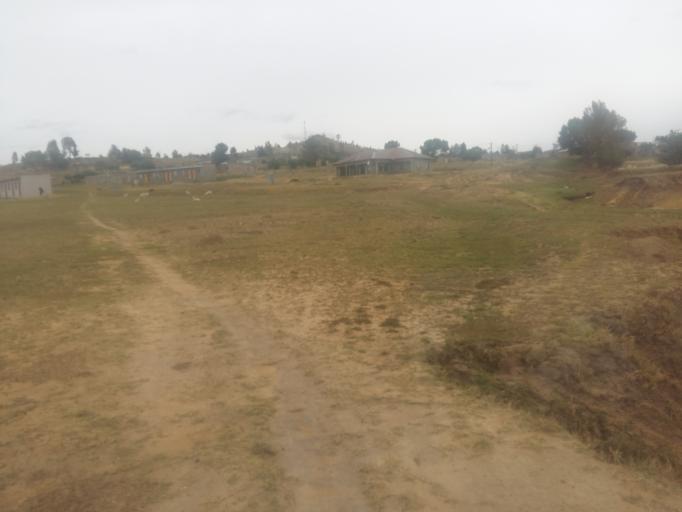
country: LS
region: Mafeteng
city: Mafeteng
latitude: -29.6974
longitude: 27.4356
